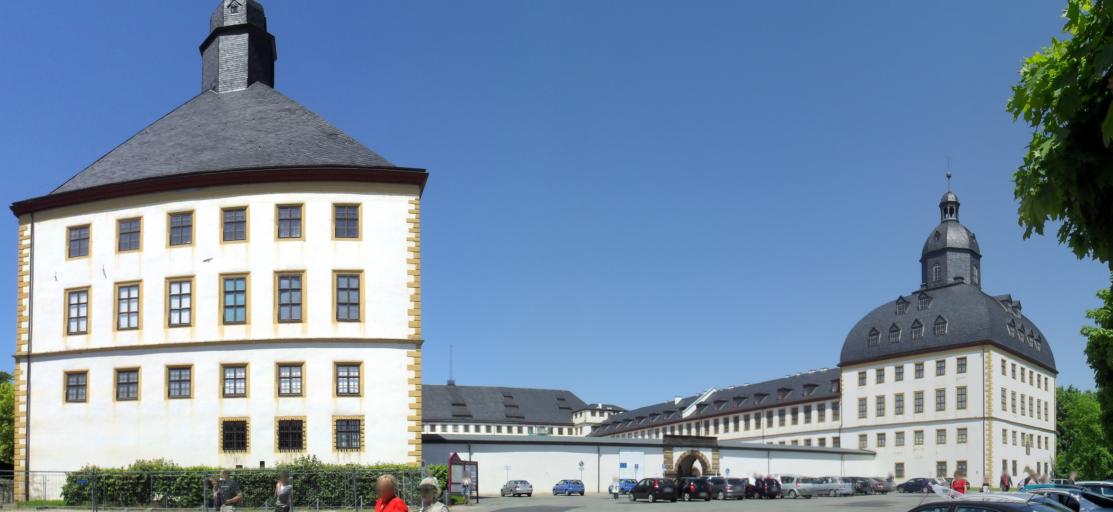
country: DE
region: Thuringia
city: Gotha
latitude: 50.9448
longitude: 10.7044
